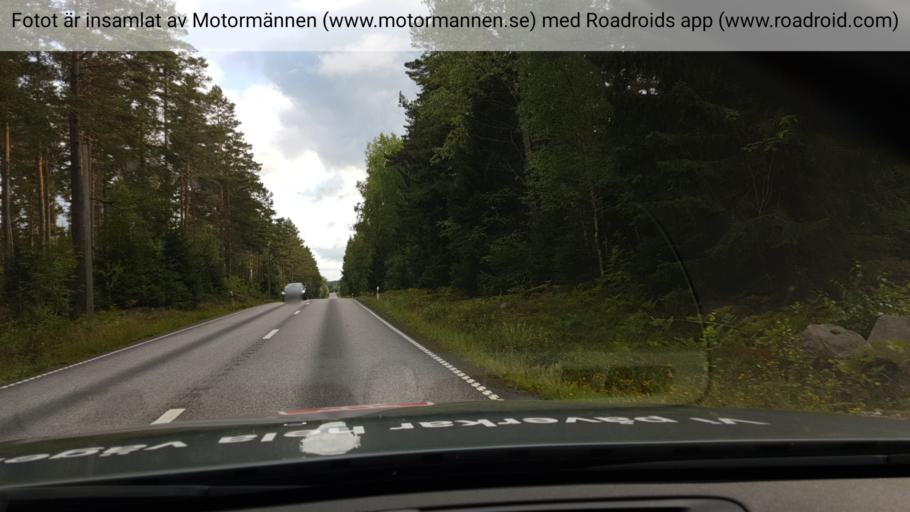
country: SE
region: Stockholm
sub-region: Norrtalje Kommun
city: Hallstavik
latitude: 59.9878
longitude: 18.5936
